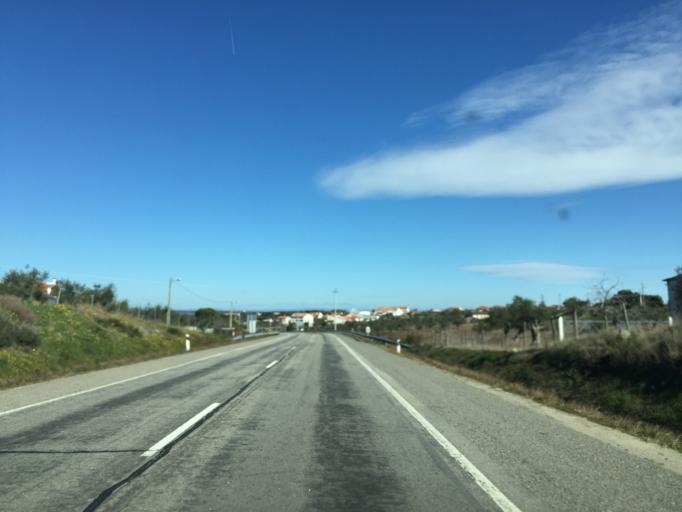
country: PT
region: Castelo Branco
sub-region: Castelo Branco
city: Castelo Branco
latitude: 39.8316
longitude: -7.5050
